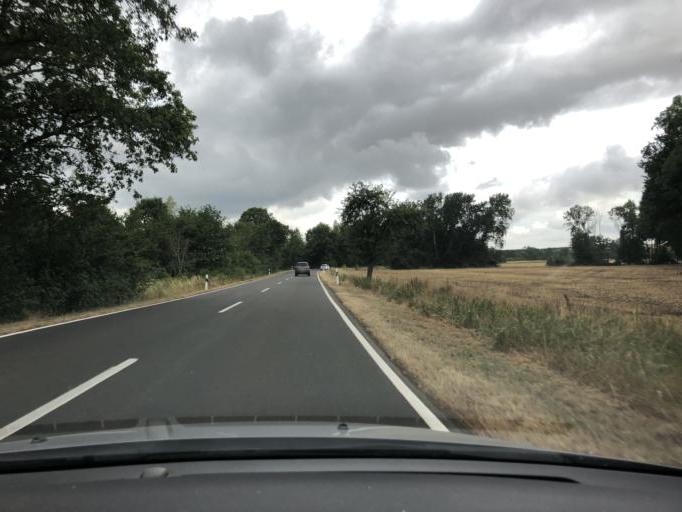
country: DE
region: Saxony-Anhalt
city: Ermlitz
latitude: 51.3881
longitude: 12.1335
